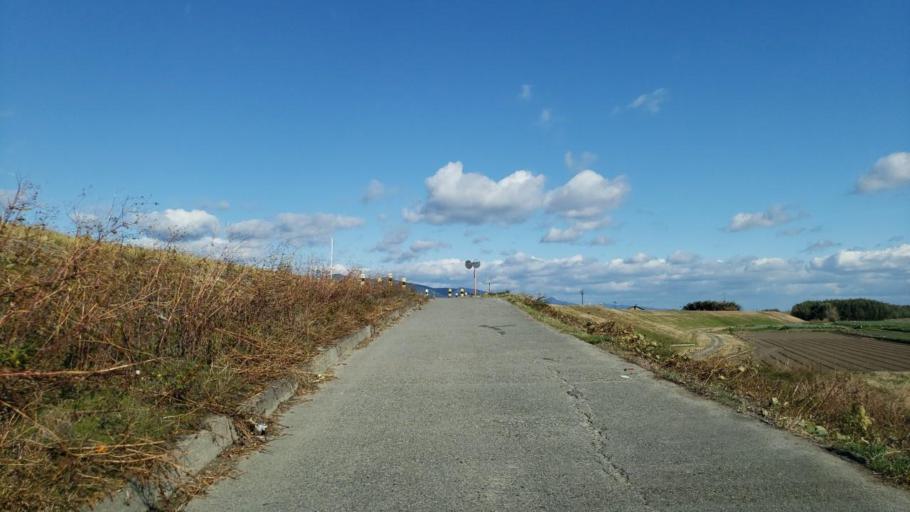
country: JP
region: Tokushima
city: Kamojimacho-jogejima
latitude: 34.0800
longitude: 134.2953
